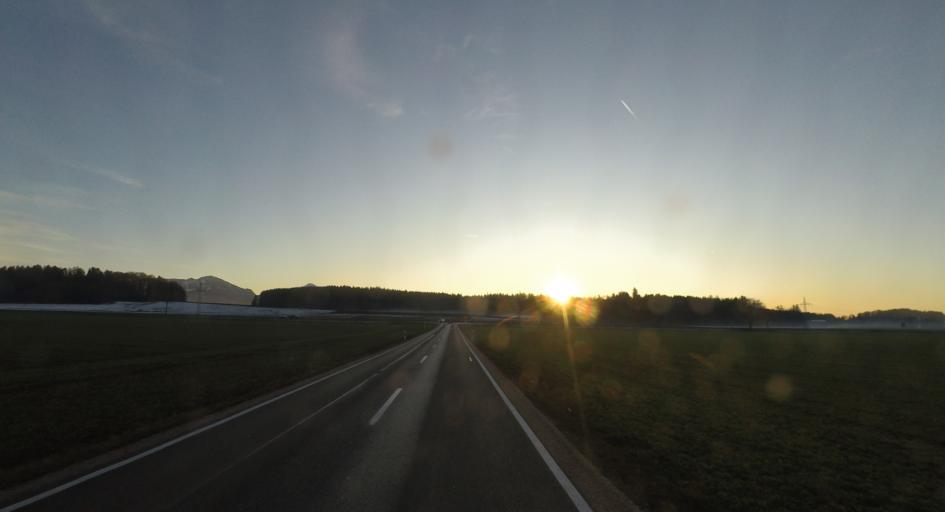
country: DE
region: Bavaria
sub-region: Upper Bavaria
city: Nussdorf
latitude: 47.8856
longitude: 12.5835
